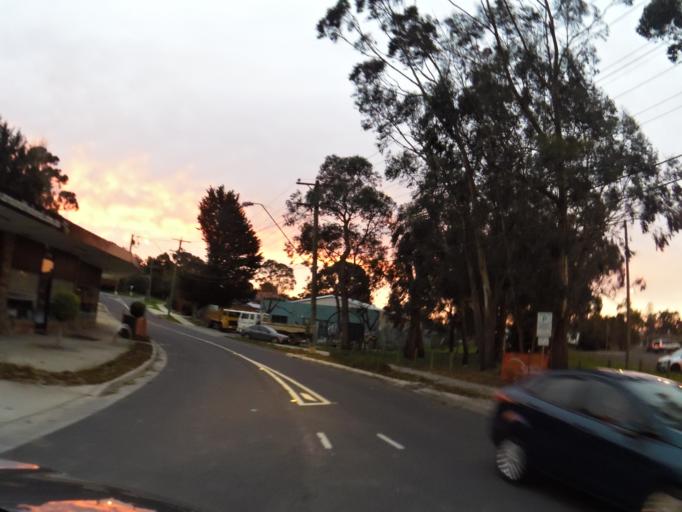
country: AU
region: Victoria
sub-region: Knox
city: Ferntree Gully
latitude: -37.8817
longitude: 145.2945
